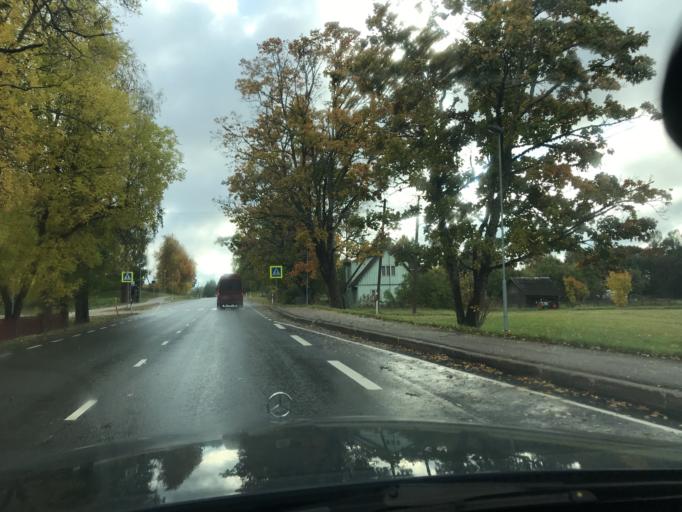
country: EE
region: Viljandimaa
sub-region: Karksi vald
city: Karksi-Nuia
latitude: 58.0122
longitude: 25.6945
